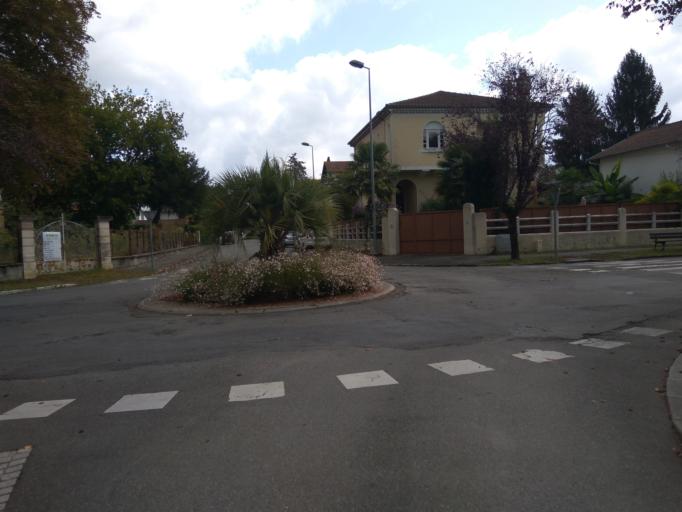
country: FR
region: Aquitaine
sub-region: Departement des Pyrenees-Atlantiques
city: Bizanos
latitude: 43.3010
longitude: -0.3478
